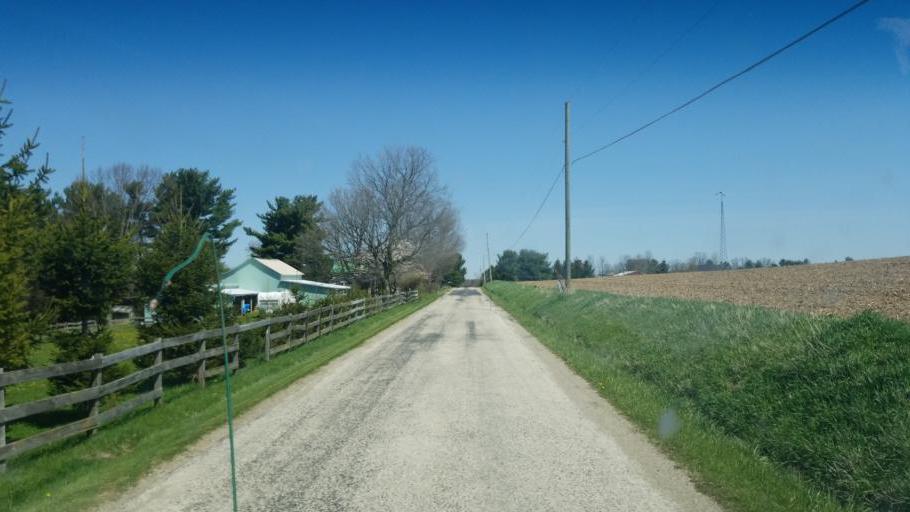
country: US
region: Ohio
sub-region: Ashland County
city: Ashland
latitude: 40.8692
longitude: -82.4161
